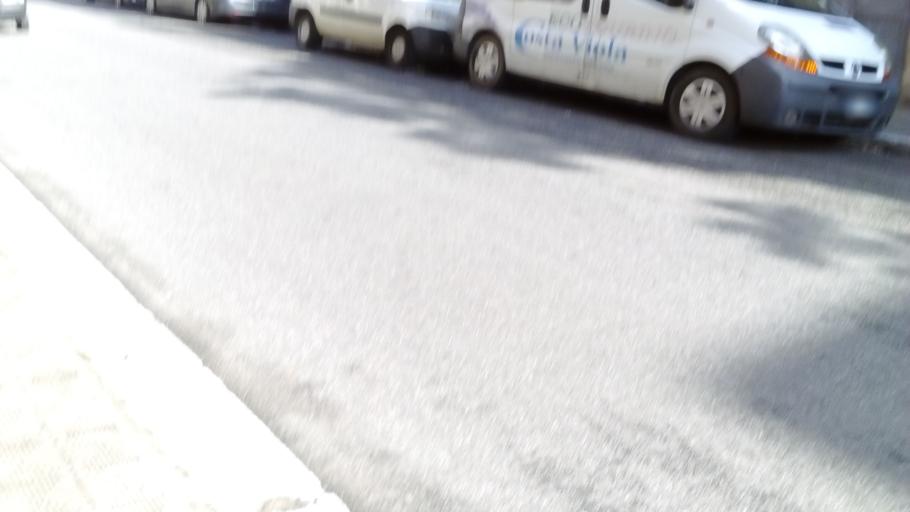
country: IT
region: Calabria
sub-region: Provincia di Reggio Calabria
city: Campo Calabro
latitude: 38.2142
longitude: 15.6380
